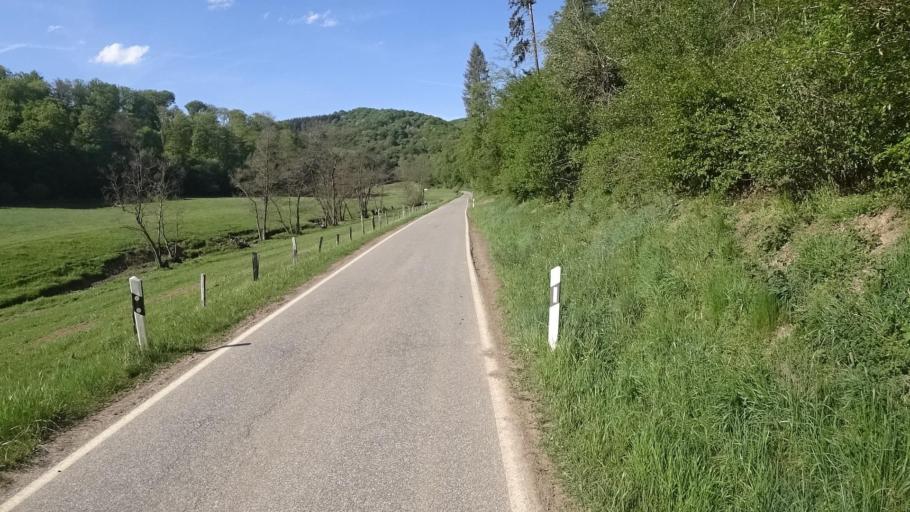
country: DE
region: Rheinland-Pfalz
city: Sierscheid
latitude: 50.4790
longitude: 6.9159
